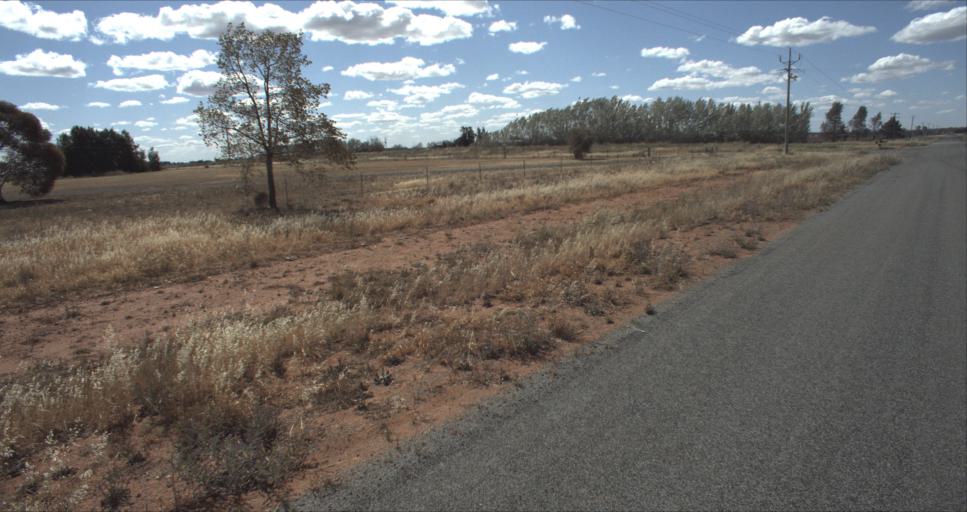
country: AU
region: New South Wales
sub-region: Leeton
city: Leeton
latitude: -34.4601
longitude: 146.2529
